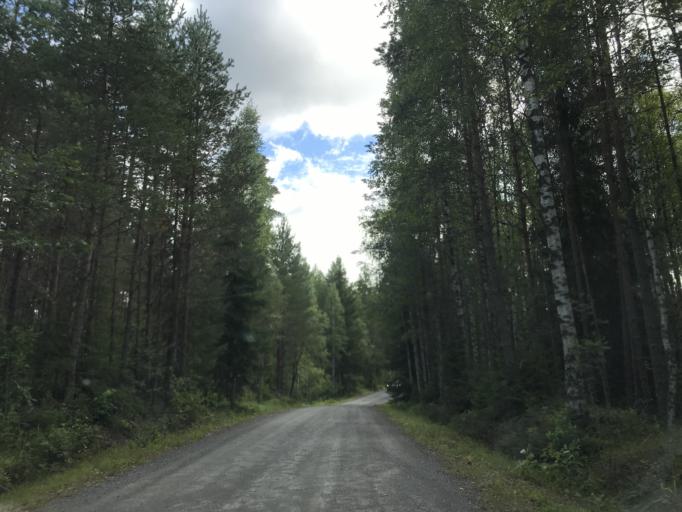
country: FI
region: Uusimaa
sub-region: Helsinki
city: Kaerkoelae
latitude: 60.6374
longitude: 23.7864
